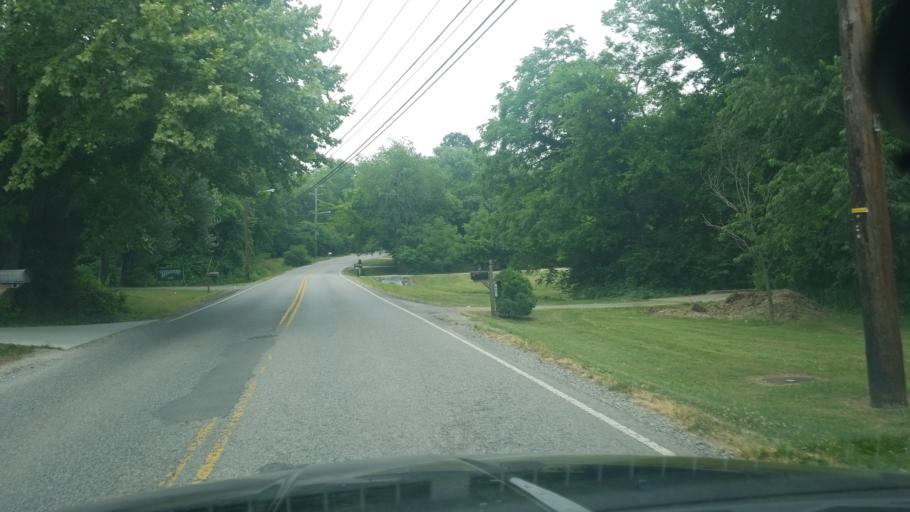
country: US
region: Tennessee
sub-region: Davidson County
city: Goodlettsville
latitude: 36.2552
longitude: -86.7480
